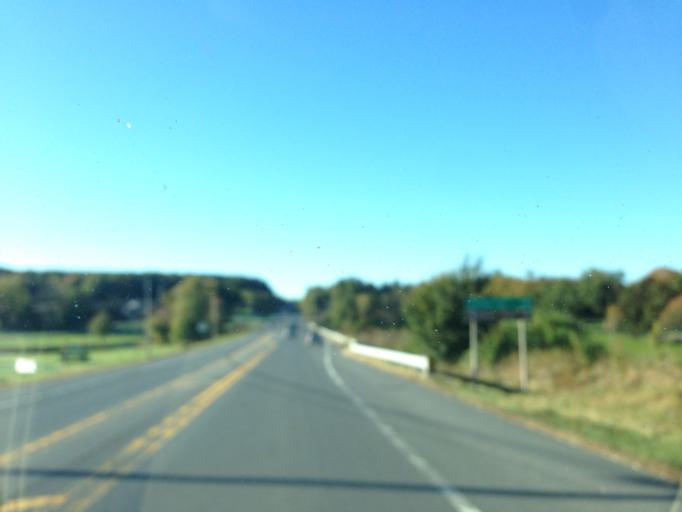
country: US
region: Maryland
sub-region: Carroll County
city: Mount Airy
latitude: 39.3775
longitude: -77.1439
